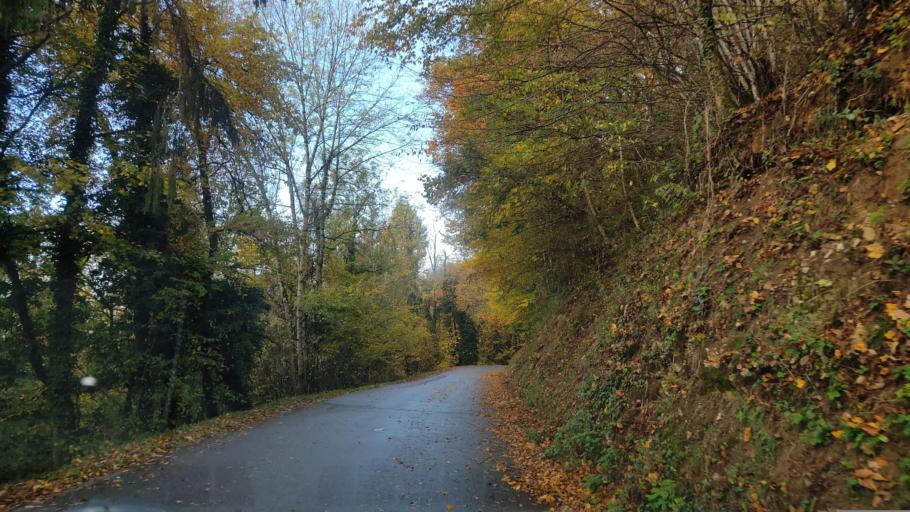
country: FR
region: Rhone-Alpes
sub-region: Departement de la Savoie
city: Novalaise
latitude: 45.6038
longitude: 5.7922
